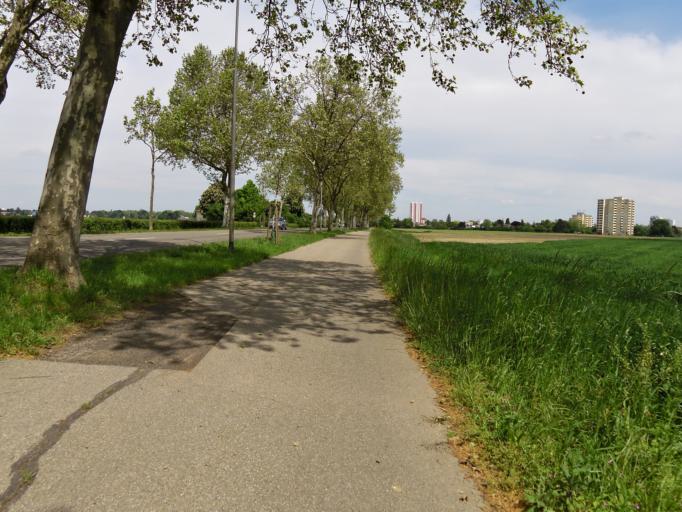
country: DE
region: Rheinland-Pfalz
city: Frankenthal
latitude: 49.5191
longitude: 8.3376
